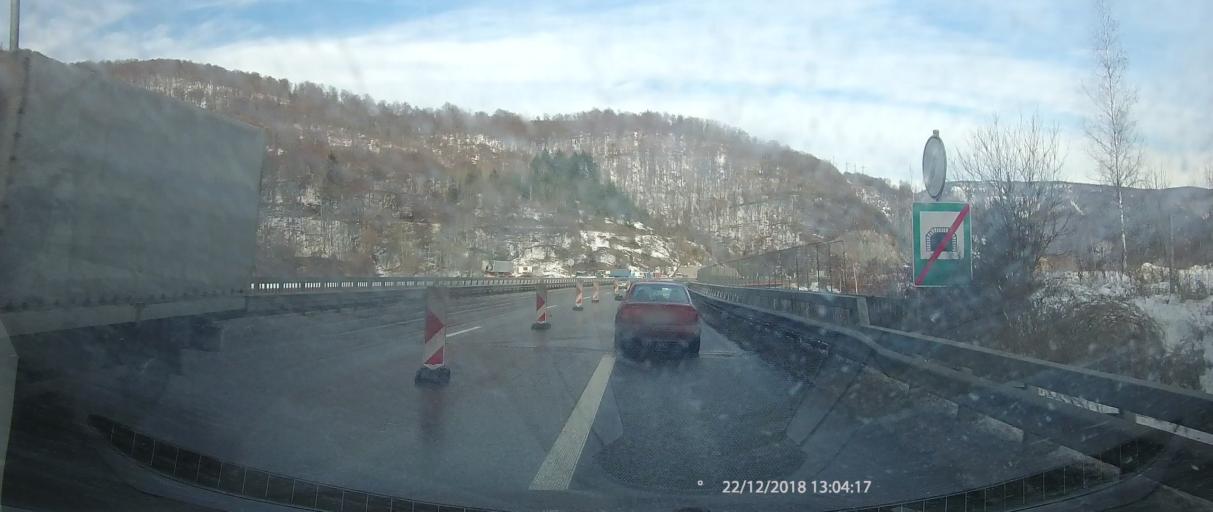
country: BG
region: Sofiya
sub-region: Obshtina Botevgrad
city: Botevgrad
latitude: 42.7880
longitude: 23.7965
